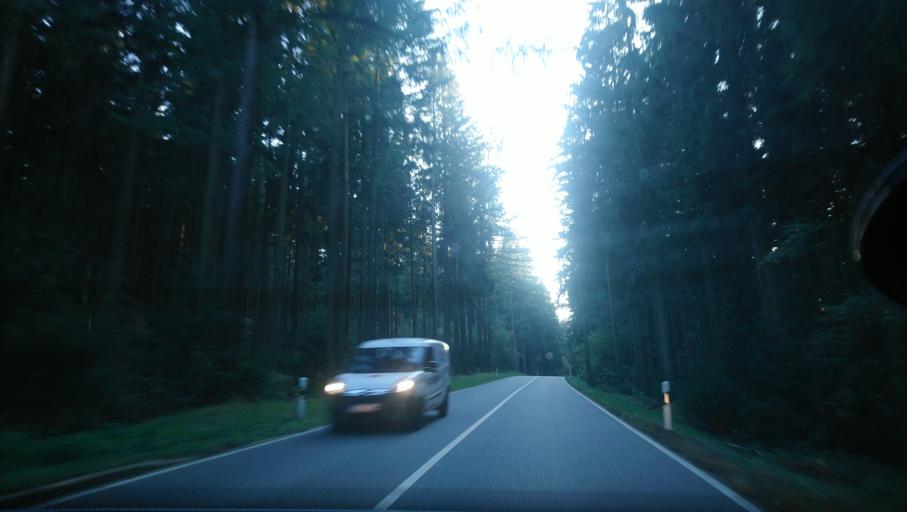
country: DE
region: Saxony
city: Thum
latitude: 50.6540
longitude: 12.9446
